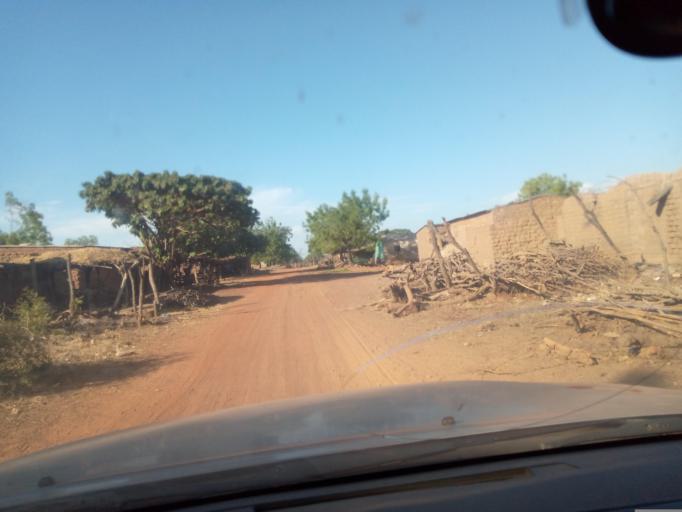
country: ML
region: Sikasso
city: Sikasso
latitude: 11.4842
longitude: -5.4813
